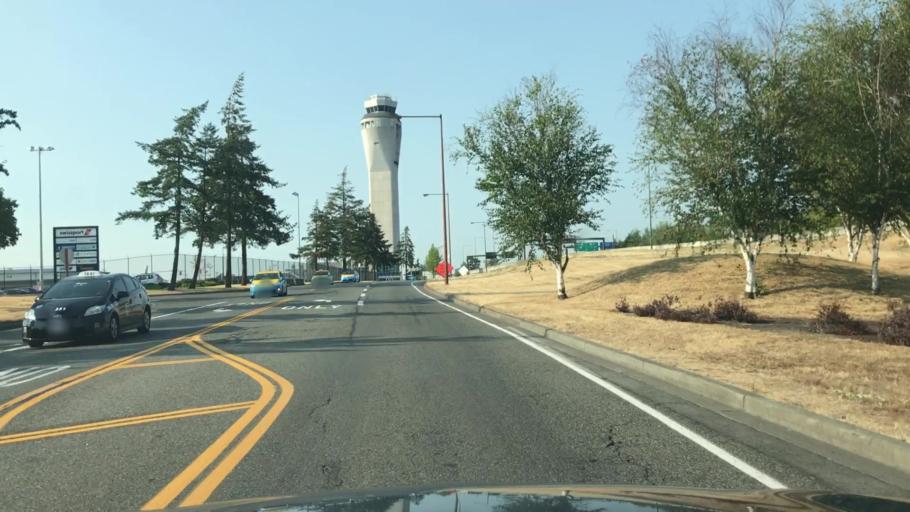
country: US
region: Washington
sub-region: King County
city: SeaTac
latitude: 47.4525
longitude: -122.3015
